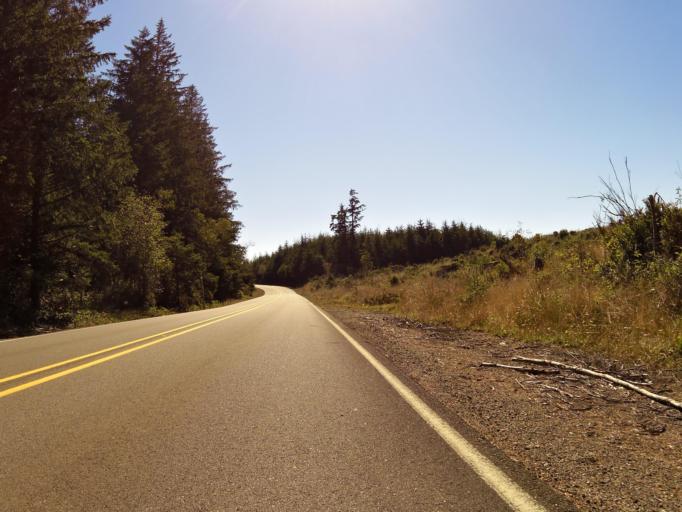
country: US
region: Oregon
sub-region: Coos County
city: Barview
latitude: 43.2530
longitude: -124.3369
